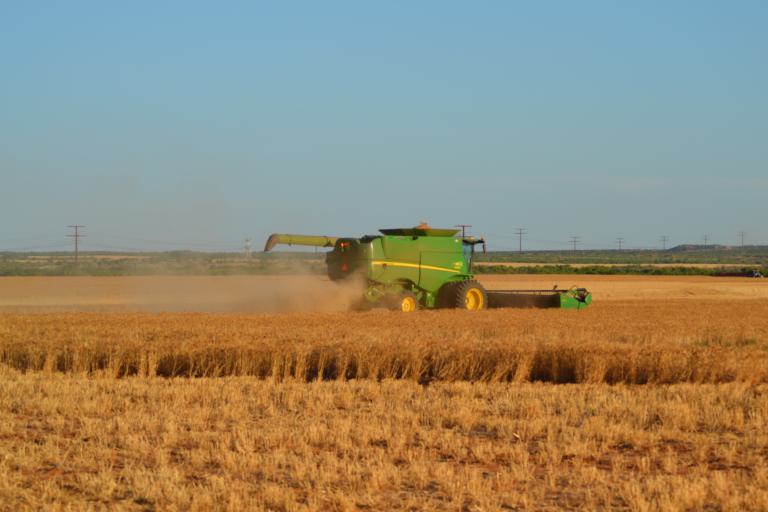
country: US
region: Texas
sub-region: Childress County
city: Childress
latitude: 34.4068
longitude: -100.1235
